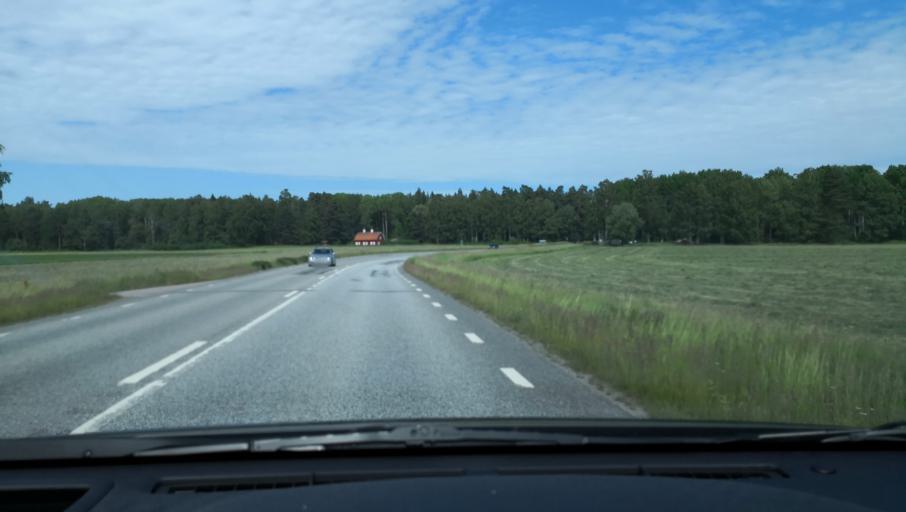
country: SE
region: Uppsala
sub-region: Uppsala Kommun
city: Saevja
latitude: 59.7681
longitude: 17.6489
